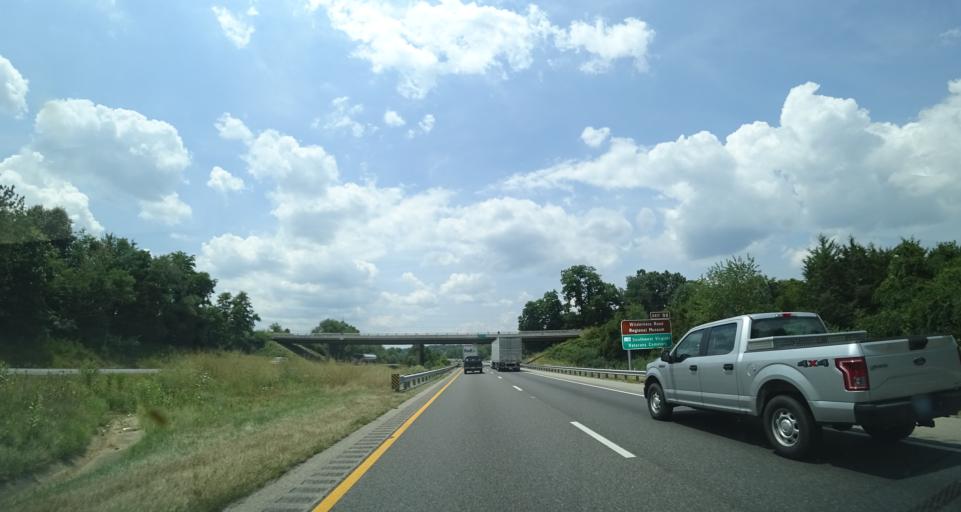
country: US
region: Virginia
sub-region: Pulaski County
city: Dublin
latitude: 37.0802
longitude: -80.6822
